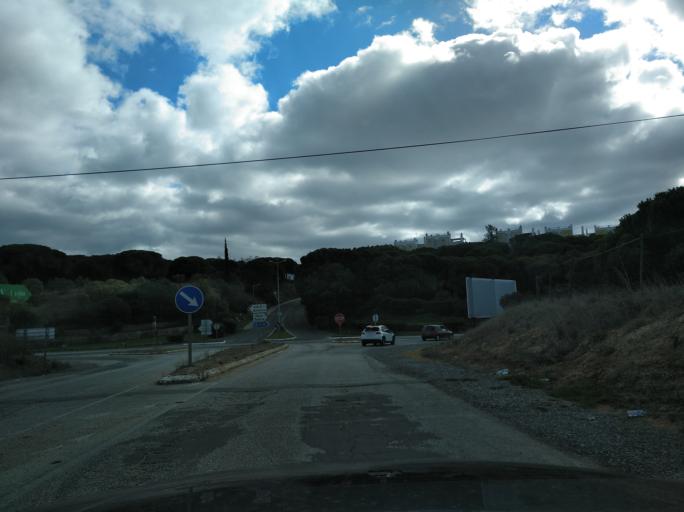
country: PT
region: Faro
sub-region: Vila Real de Santo Antonio
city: Monte Gordo
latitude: 37.1846
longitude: -7.4842
